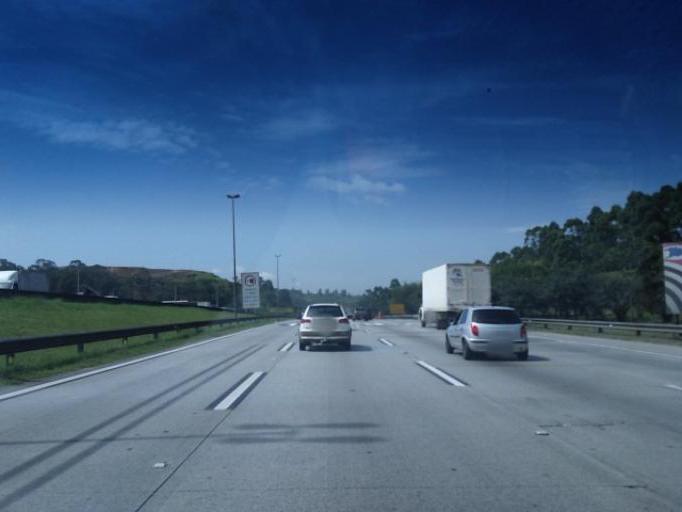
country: BR
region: Sao Paulo
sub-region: Taboao Da Serra
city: Taboao da Serra
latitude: -23.5932
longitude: -46.8107
